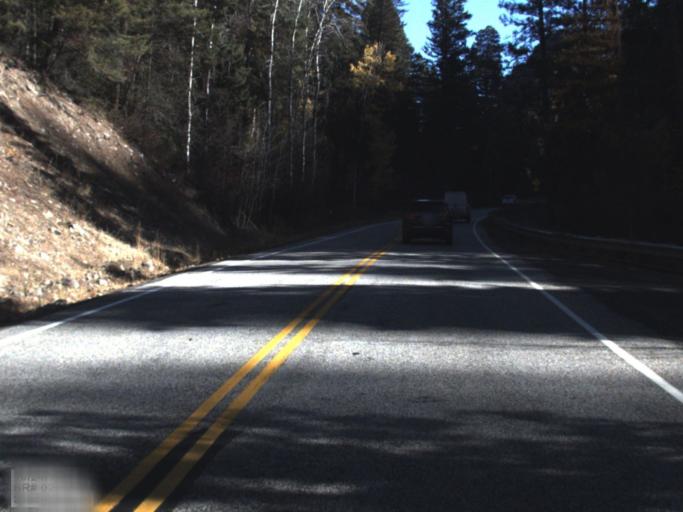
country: US
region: Washington
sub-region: Ferry County
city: Republic
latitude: 48.5991
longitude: -118.6248
